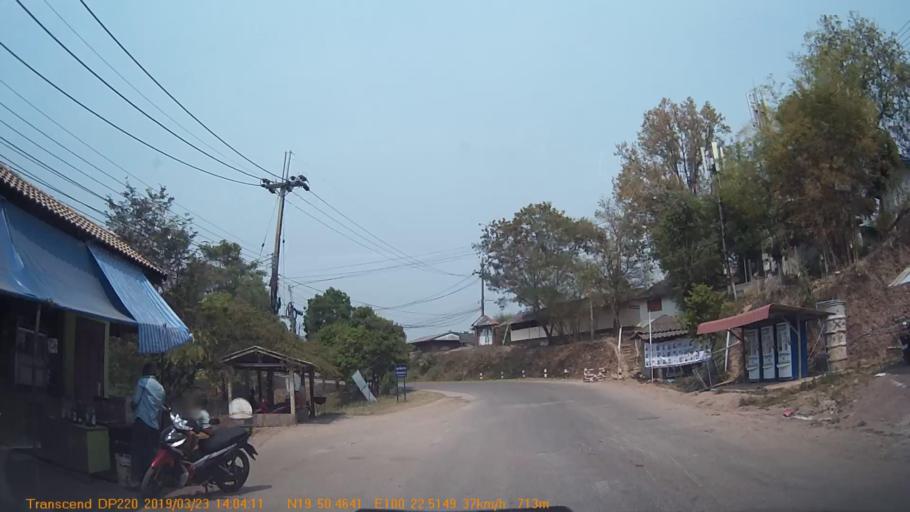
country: TH
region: Chiang Rai
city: Khun Tan
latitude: 19.8412
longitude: 100.3754
